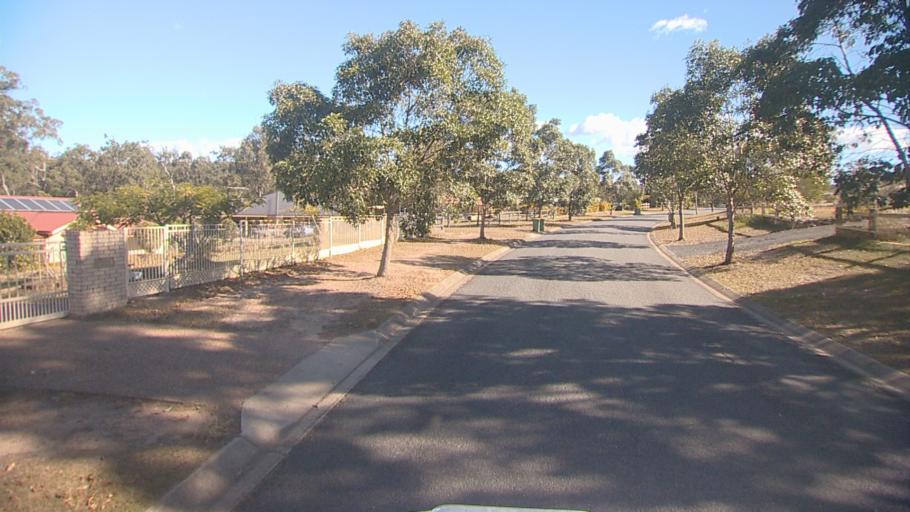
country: AU
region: Queensland
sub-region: Ipswich
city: Springfield Lakes
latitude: -27.7348
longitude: 152.9120
